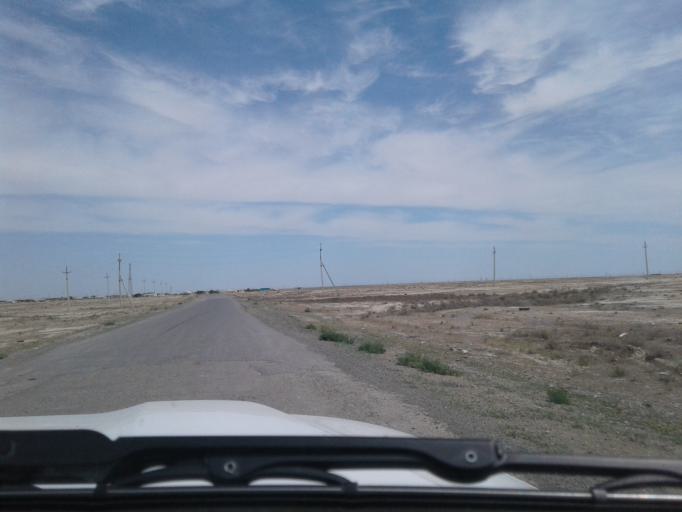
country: TM
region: Balkan
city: Gazanjyk
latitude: 39.2006
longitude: 55.7084
